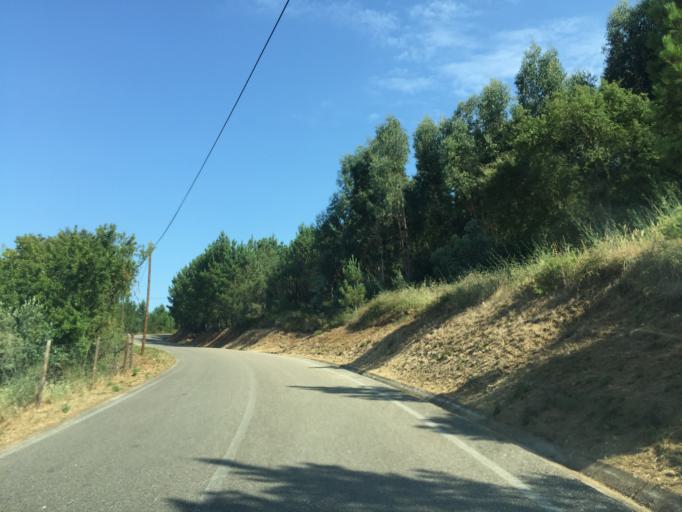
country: PT
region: Santarem
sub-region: Ferreira do Zezere
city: Ferreira do Zezere
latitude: 39.5959
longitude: -8.2994
